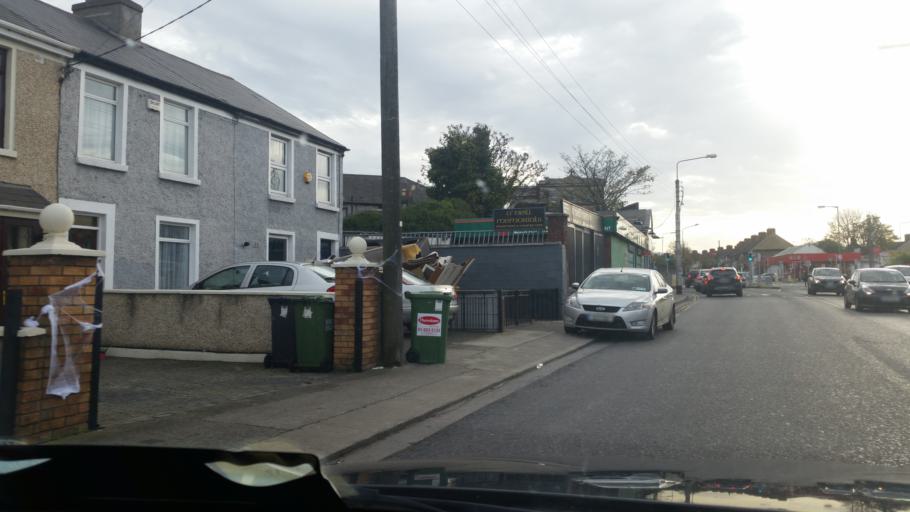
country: IE
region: Leinster
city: Rialto
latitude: 53.3310
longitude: -6.2980
